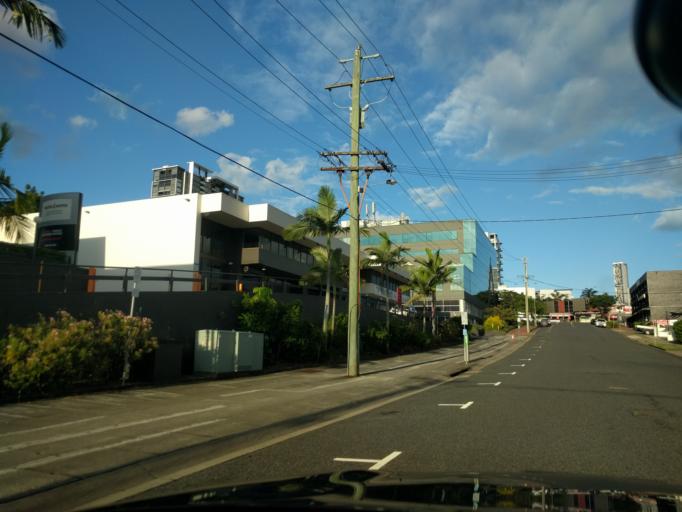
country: AU
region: Queensland
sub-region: Brisbane
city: Milton
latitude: -27.4718
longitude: 153.0033
